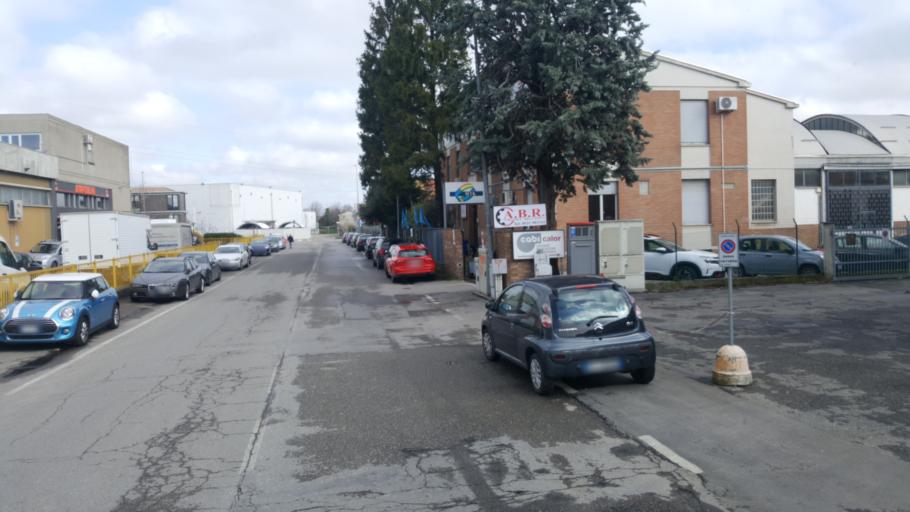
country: IT
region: Emilia-Romagna
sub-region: Provincia di Parma
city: Parma
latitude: 44.8110
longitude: 10.3069
